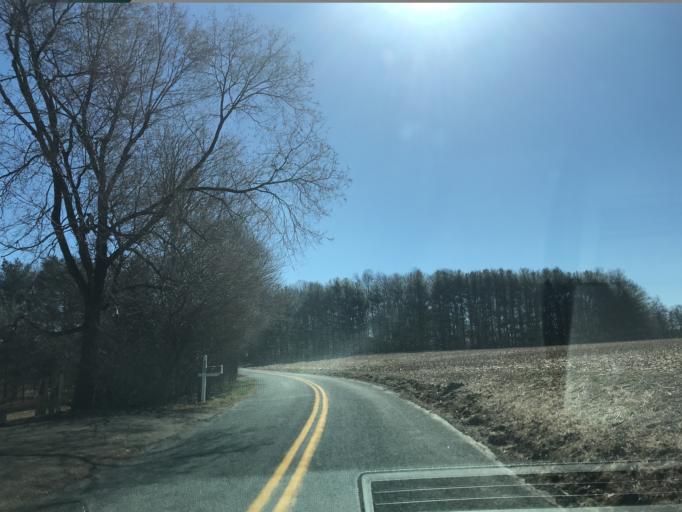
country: US
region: Pennsylvania
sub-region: York County
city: Stewartstown
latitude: 39.7118
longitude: -76.5265
